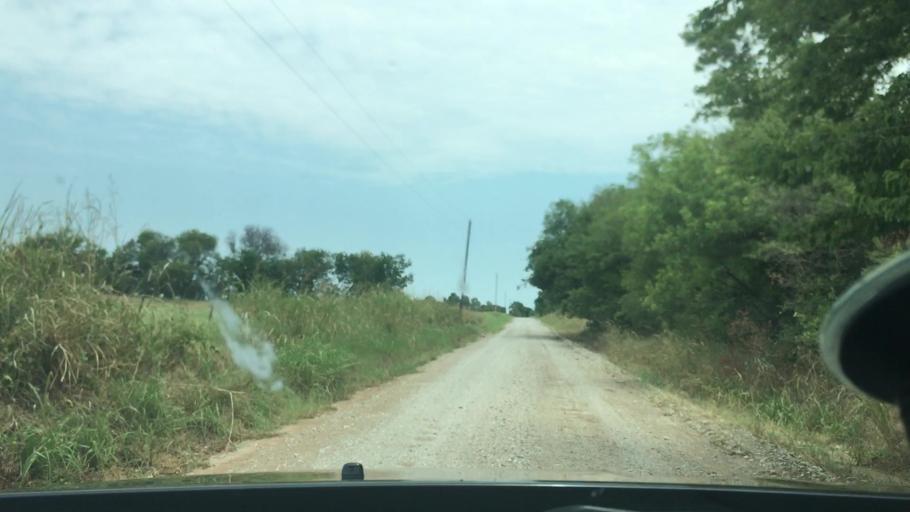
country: US
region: Texas
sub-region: Cooke County
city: Muenster
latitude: 33.8667
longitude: -97.3871
